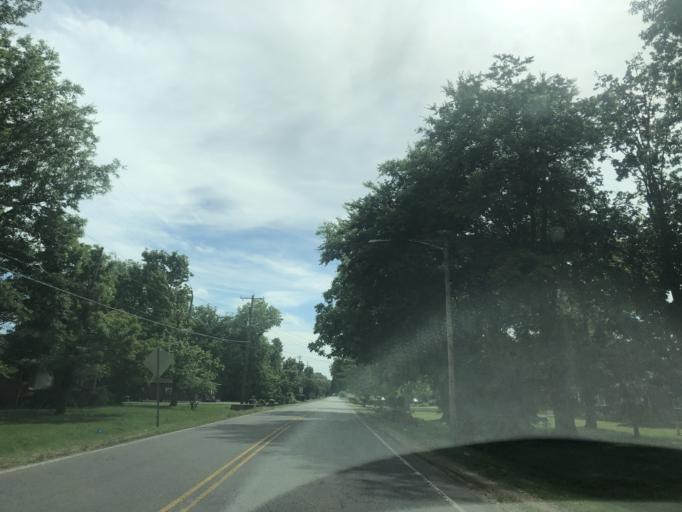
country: US
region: Tennessee
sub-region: Davidson County
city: Nashville
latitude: 36.2129
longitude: -86.8262
